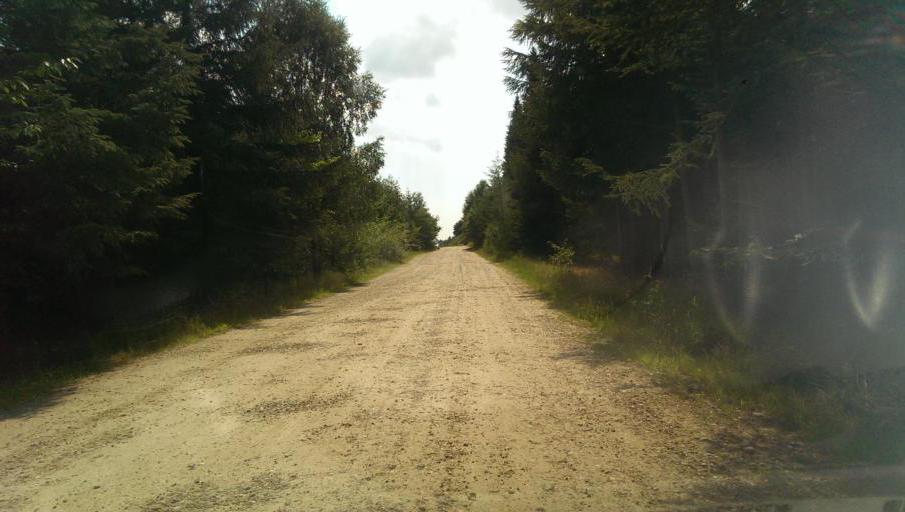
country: DK
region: South Denmark
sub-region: Varde Kommune
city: Varde
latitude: 55.5902
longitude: 8.5394
